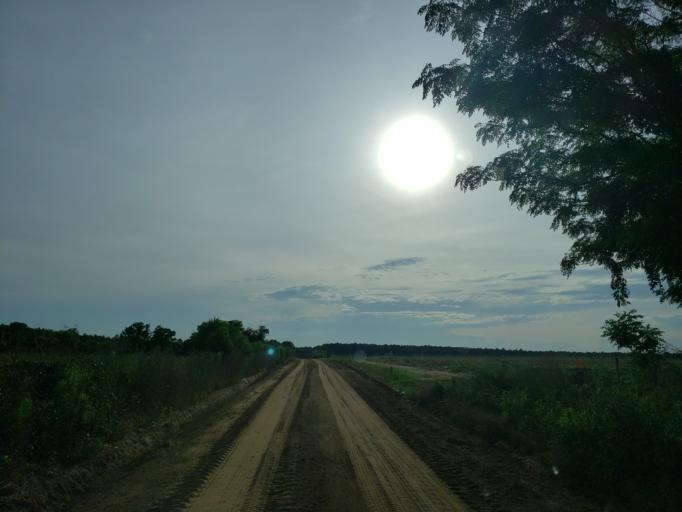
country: US
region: Georgia
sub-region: Dooly County
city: Vienna
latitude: 32.1279
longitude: -83.7696
